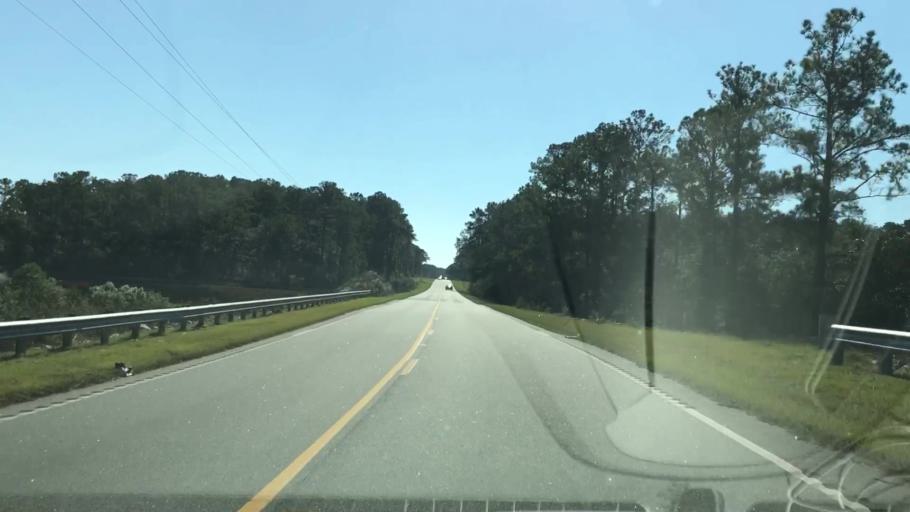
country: US
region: South Carolina
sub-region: Jasper County
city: Ridgeland
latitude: 32.4522
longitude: -80.8994
